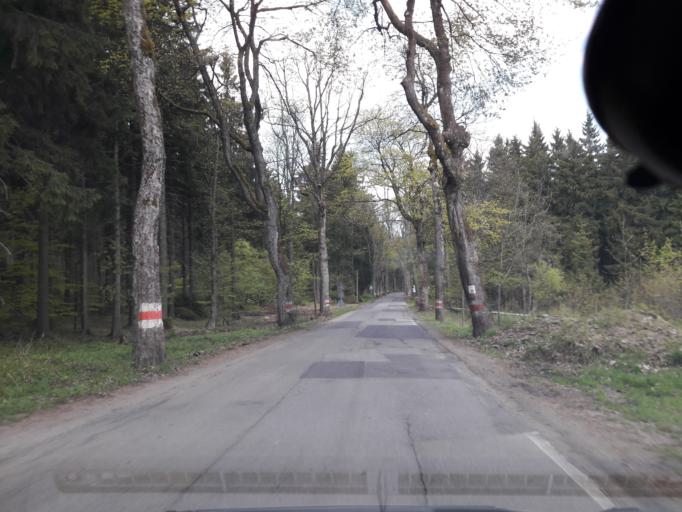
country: PL
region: Lower Silesian Voivodeship
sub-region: Powiat klodzki
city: Radkow
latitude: 50.4697
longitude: 16.3415
